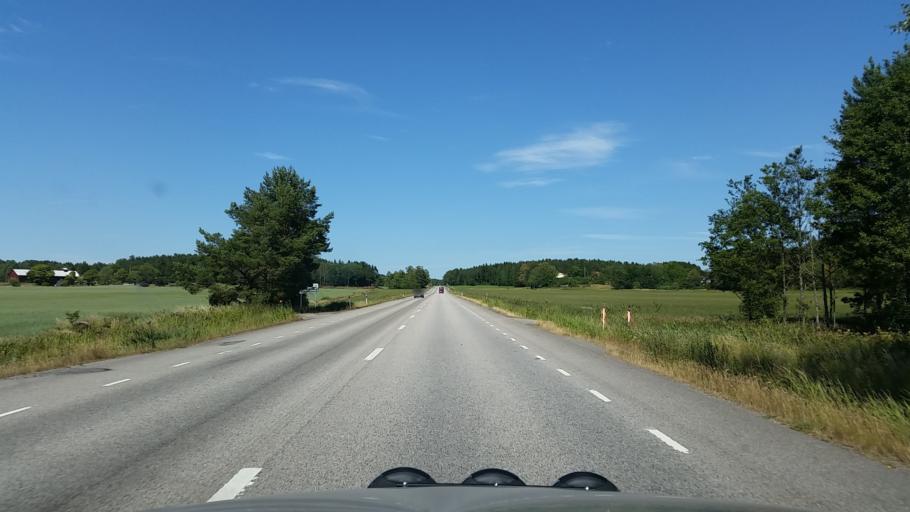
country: SE
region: Vaestra Goetaland
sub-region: Amals Kommun
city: Amal
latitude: 59.0012
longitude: 12.6831
